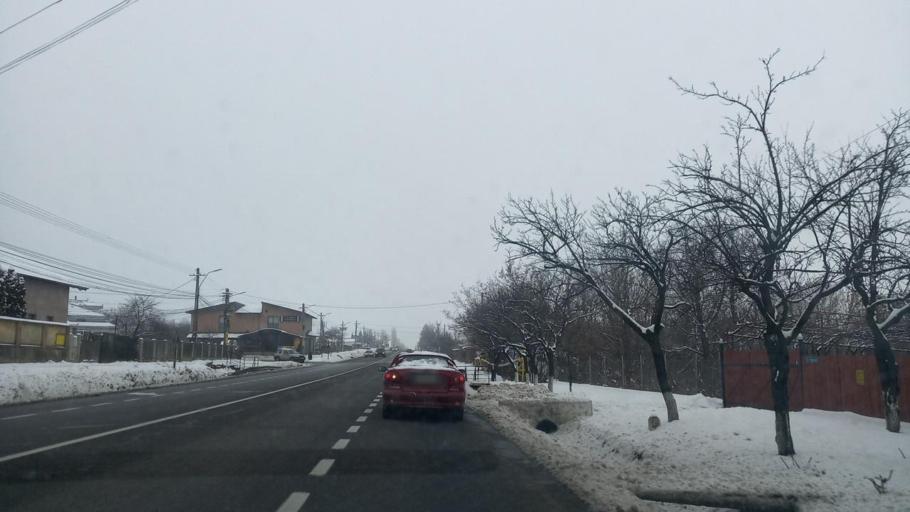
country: RO
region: Bacau
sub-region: Comuna Racaciuni
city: Gheorghe Doja
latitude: 46.4019
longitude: 26.9444
